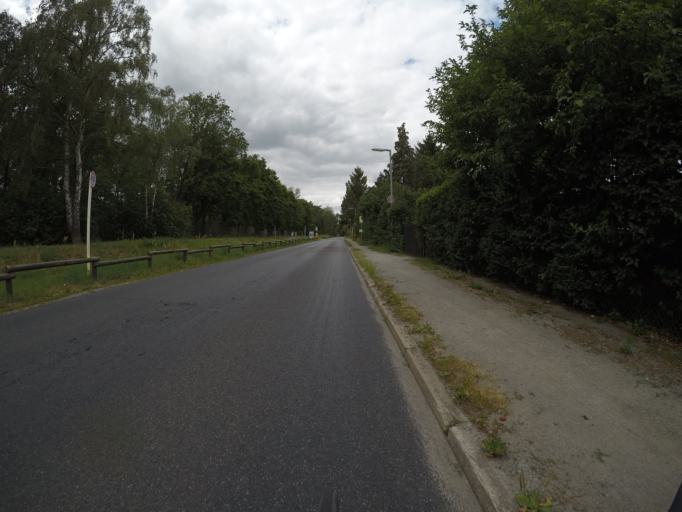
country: DE
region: Berlin
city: Falkenhagener Feld
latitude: 52.5626
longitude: 13.1665
